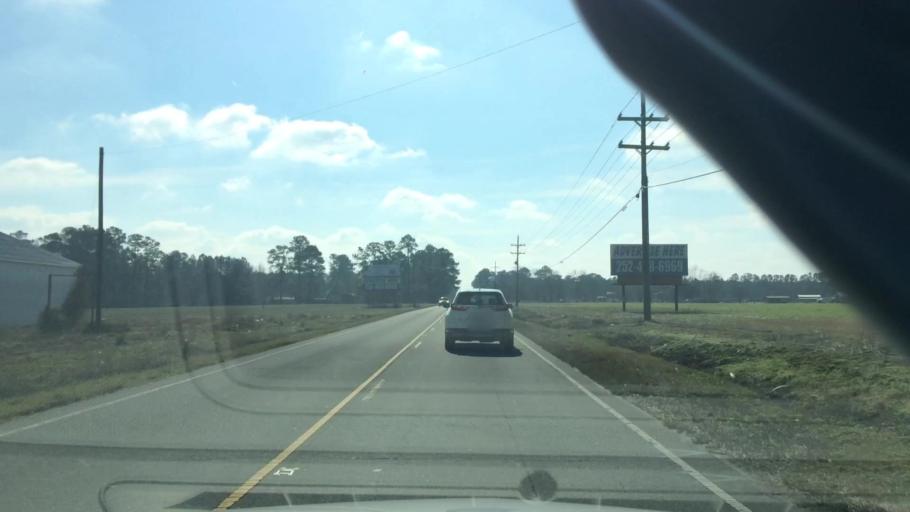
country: US
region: North Carolina
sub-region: Duplin County
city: Beulaville
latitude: 34.9040
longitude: -77.7792
